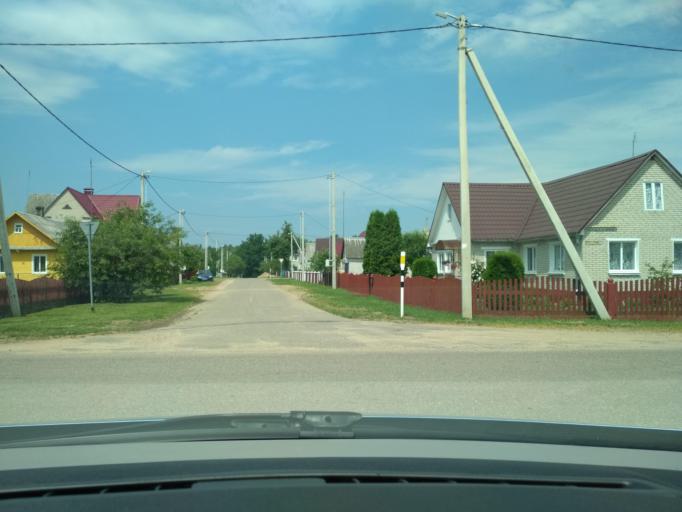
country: BY
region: Grodnenskaya
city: Astravyets
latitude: 54.6172
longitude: 25.9425
